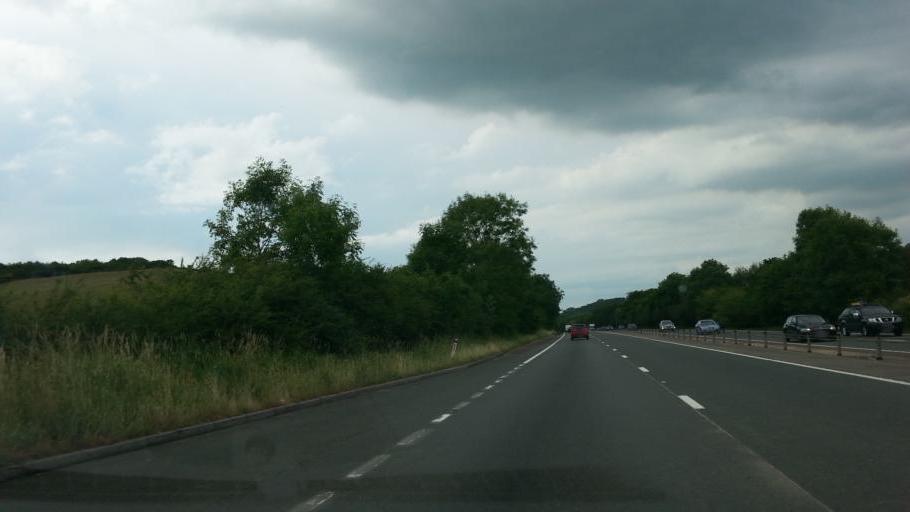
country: GB
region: Wales
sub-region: Monmouthshire
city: Llangybi
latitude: 51.6743
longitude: -2.8769
